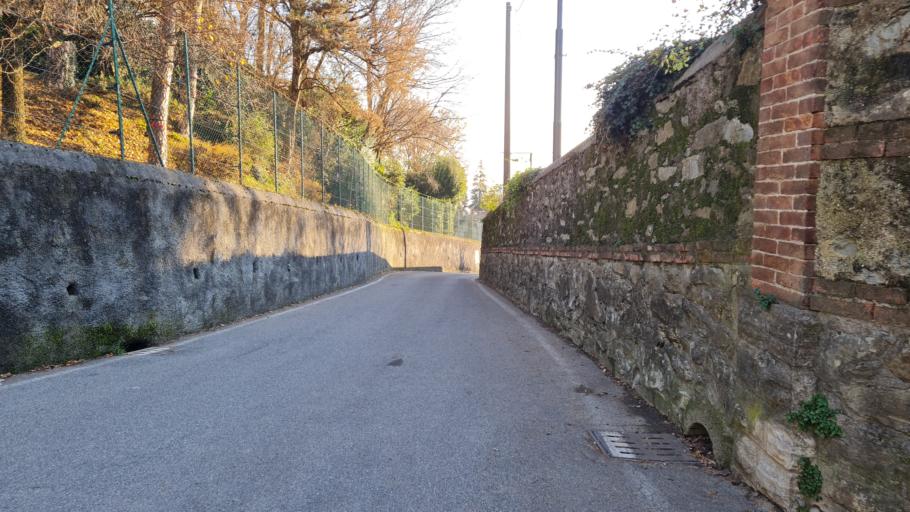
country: IT
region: Lombardy
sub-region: Provincia di Lecco
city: Vercurago
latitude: 45.8055
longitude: 9.4312
